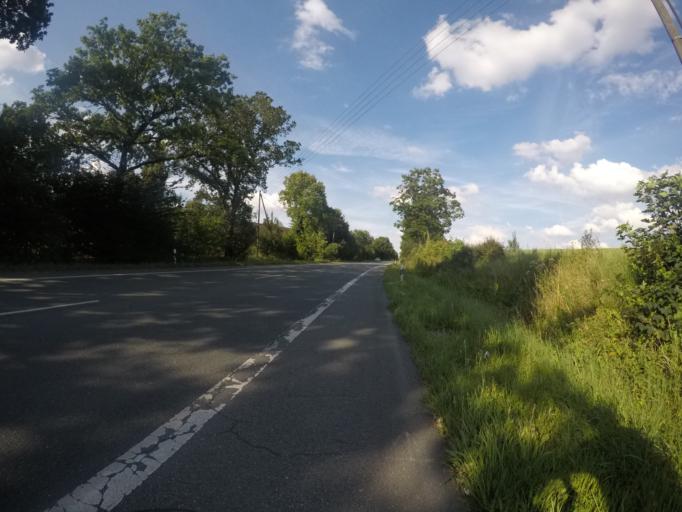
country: DE
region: North Rhine-Westphalia
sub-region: Regierungsbezirk Detmold
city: Bielefeld
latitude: 52.0660
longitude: 8.5706
